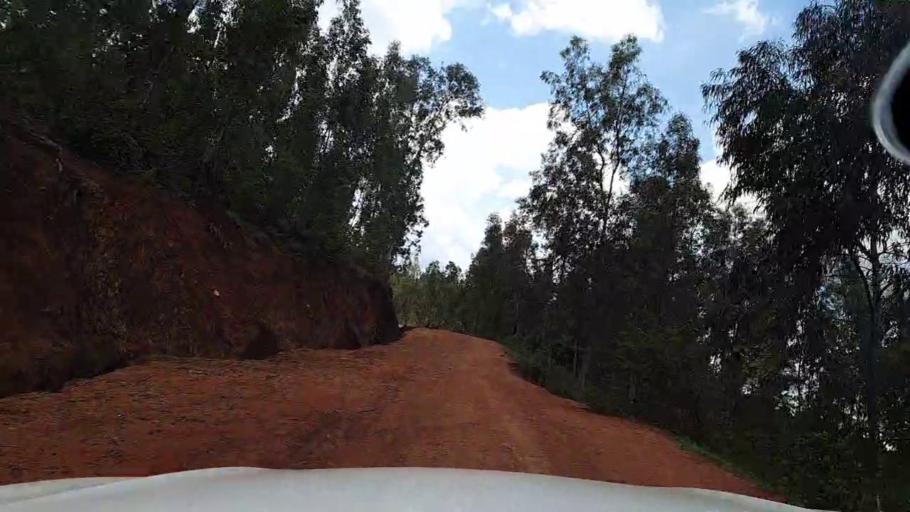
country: RW
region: Southern Province
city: Butare
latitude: -2.7444
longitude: 29.7656
